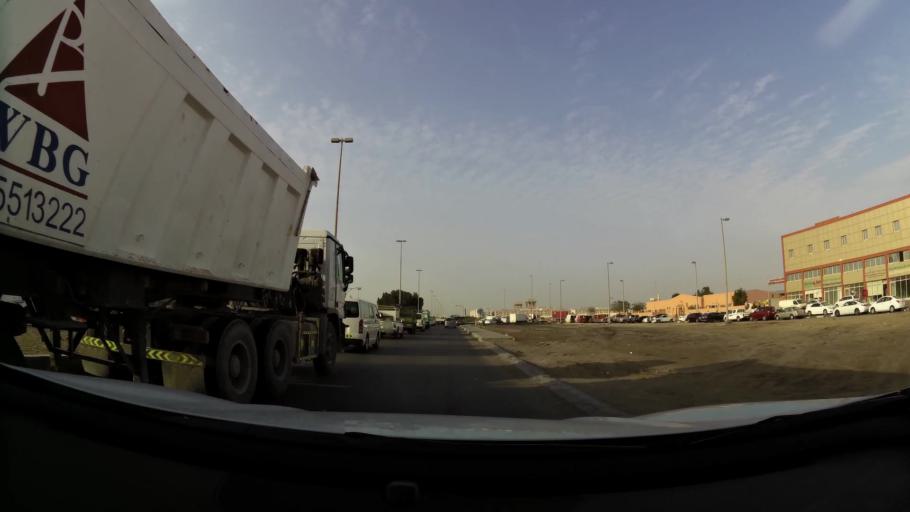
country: AE
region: Abu Dhabi
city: Abu Dhabi
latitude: 24.3540
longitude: 54.5169
